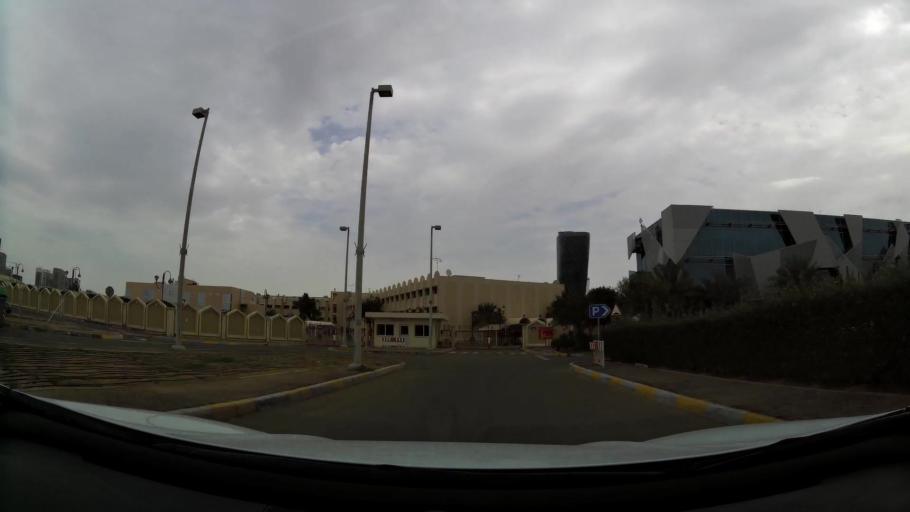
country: AE
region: Abu Dhabi
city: Abu Dhabi
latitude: 24.4210
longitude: 54.4278
